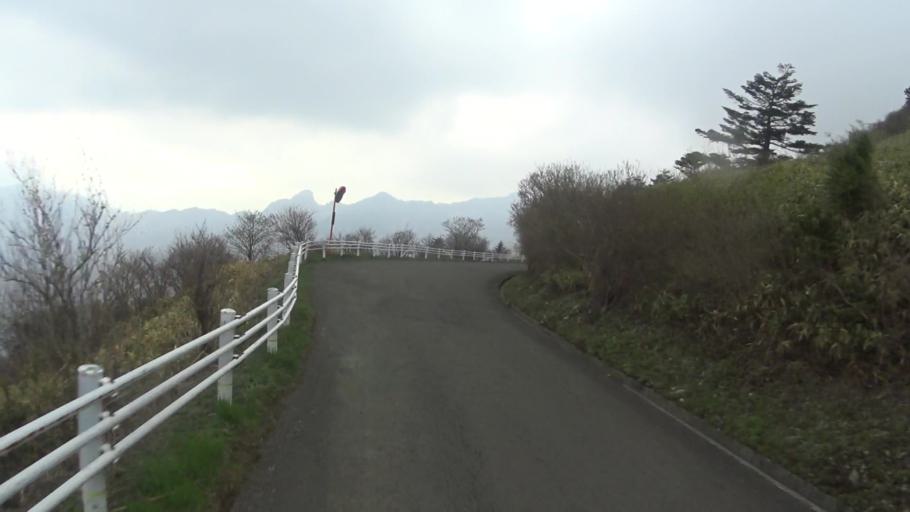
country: JP
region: Ehime
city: Saijo
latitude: 33.7788
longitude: 133.2197
